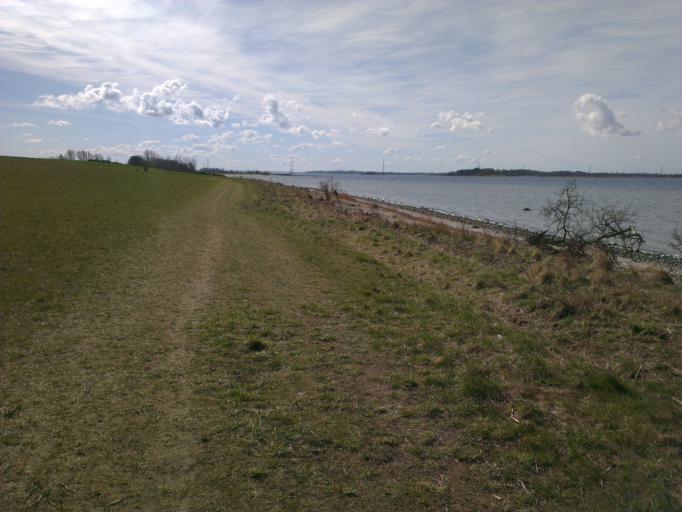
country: DK
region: Capital Region
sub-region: Frederikssund Kommune
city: Frederikssund
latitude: 55.8158
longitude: 12.0681
